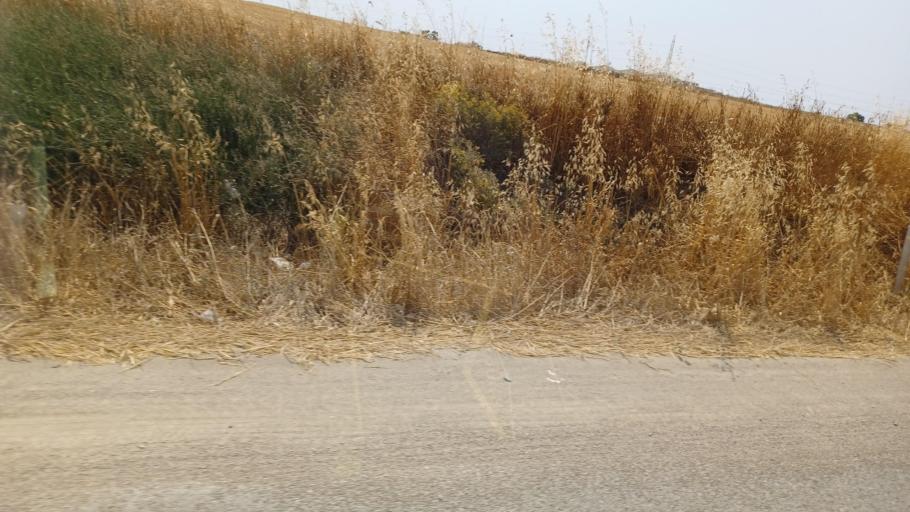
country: CY
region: Larnaka
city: Livadia
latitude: 34.9629
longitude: 33.6101
